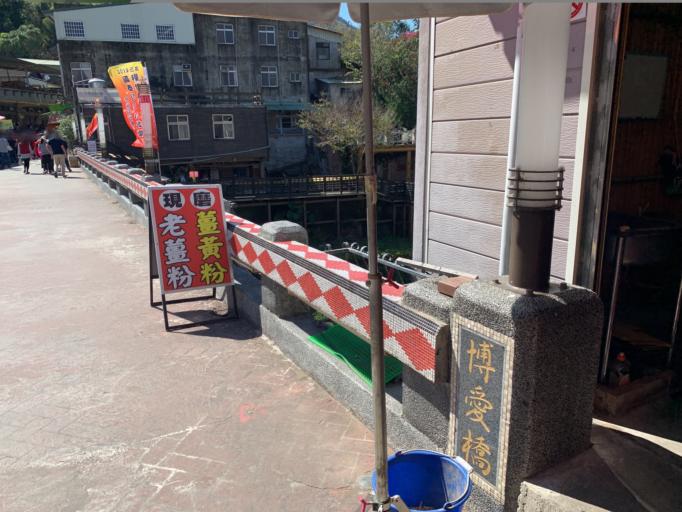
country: TW
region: Taiwan
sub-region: Miaoli
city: Miaoli
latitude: 24.4470
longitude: 120.9055
